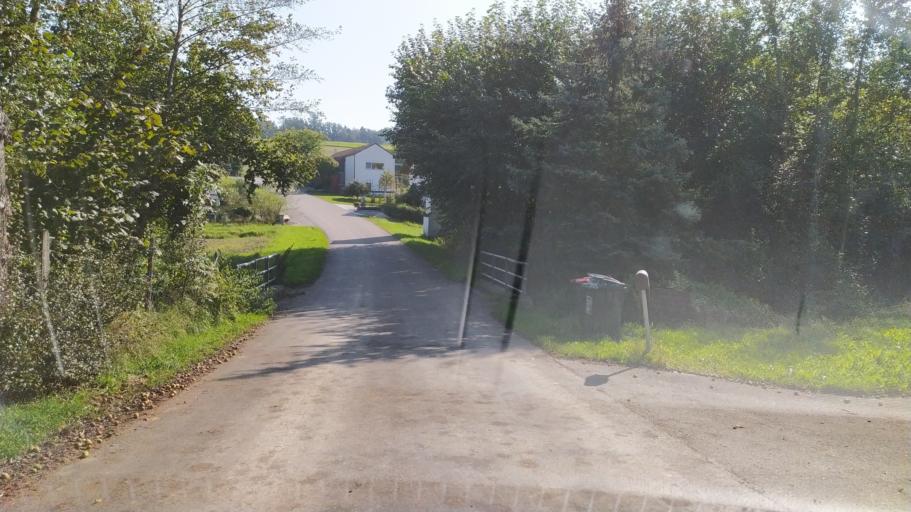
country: AT
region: Lower Austria
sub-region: Politischer Bezirk Amstetten
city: Zeillern
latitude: 48.1070
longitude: 14.7499
